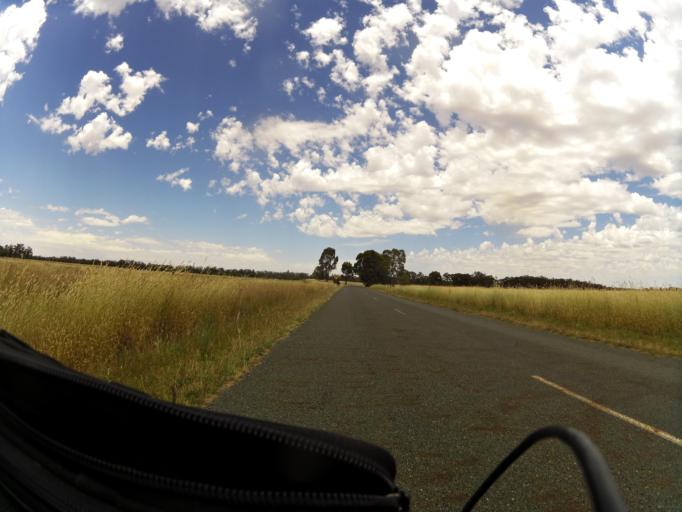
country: AU
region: Victoria
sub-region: Greater Shepparton
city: Shepparton
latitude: -36.6757
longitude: 145.1970
